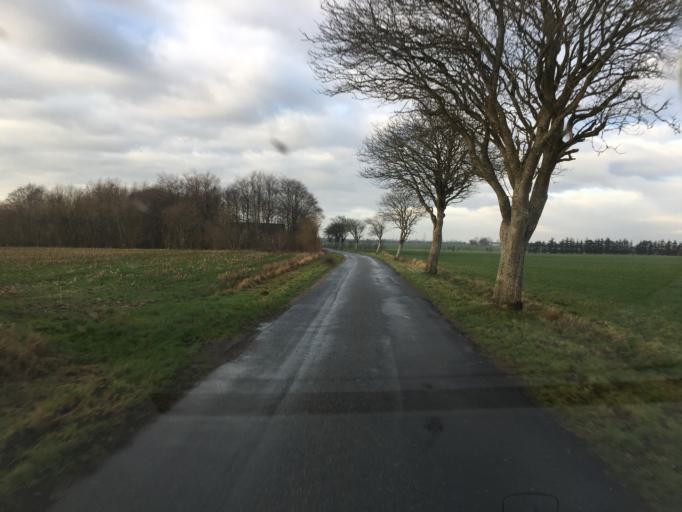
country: DK
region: South Denmark
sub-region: Tonder Kommune
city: Logumkloster
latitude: 55.1153
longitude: 8.8710
